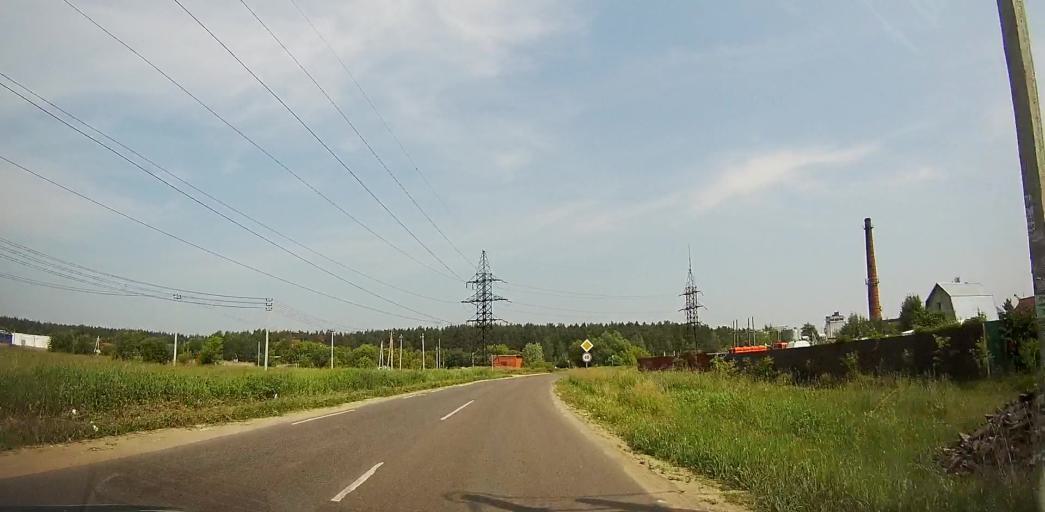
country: RU
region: Moskovskaya
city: Malyshevo
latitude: 55.5039
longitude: 38.3225
